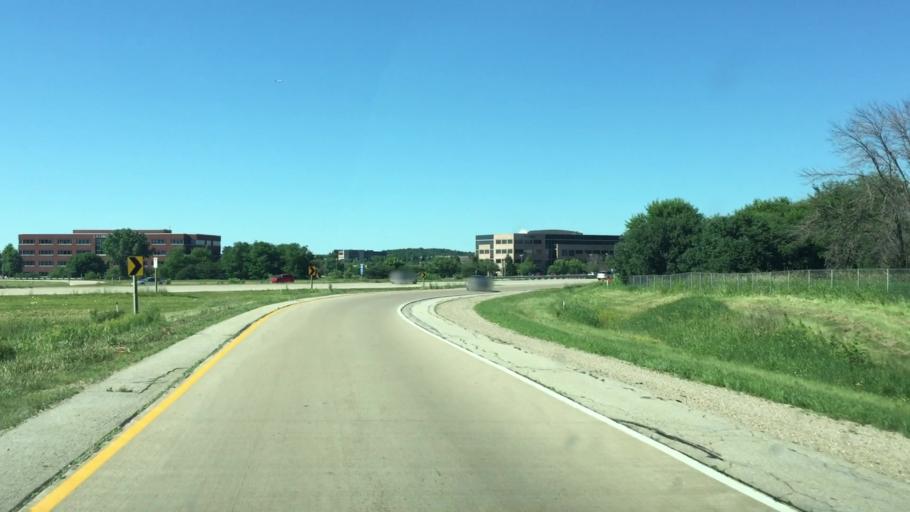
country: US
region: Wisconsin
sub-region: Dane County
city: Monona
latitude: 43.1381
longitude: -89.2934
